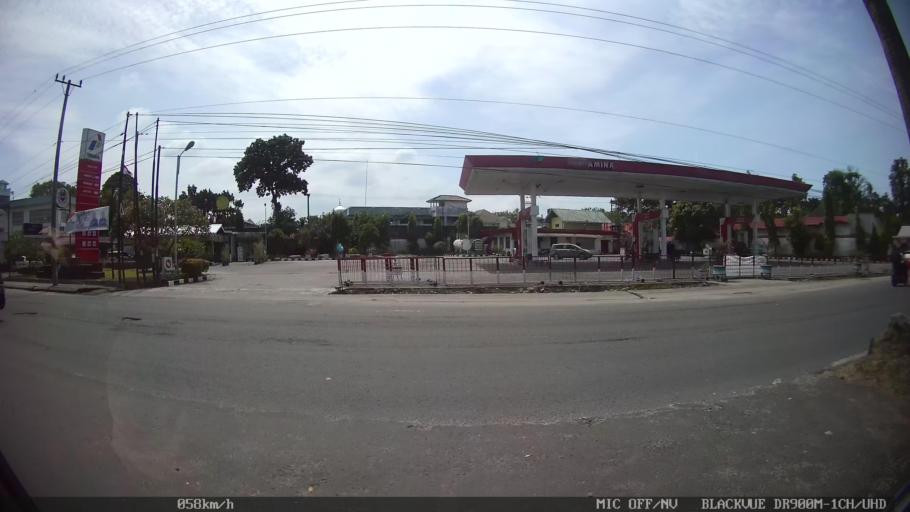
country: ID
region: North Sumatra
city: Medan
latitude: 3.5878
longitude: 98.6424
